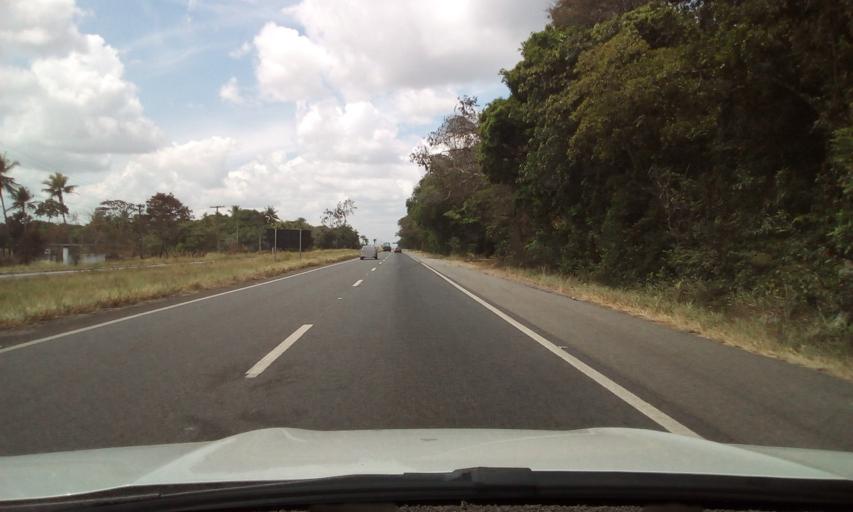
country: BR
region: Paraiba
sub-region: Santa Rita
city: Santa Rita
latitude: -7.1469
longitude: -35.0015
